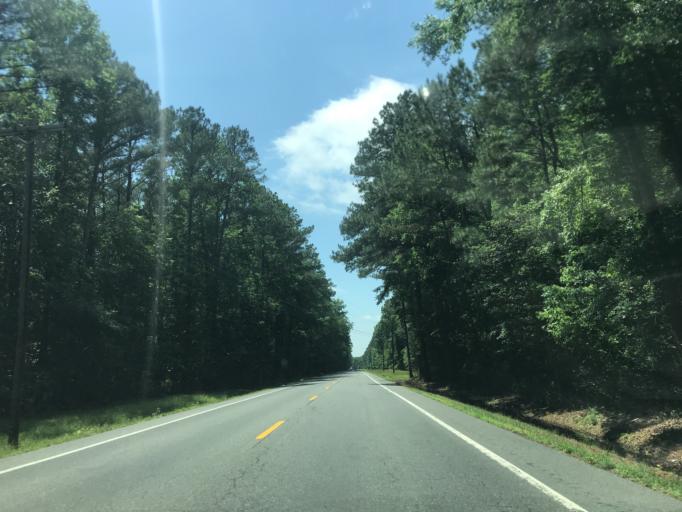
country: US
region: Maryland
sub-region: Dorchester County
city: Hurlock
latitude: 38.6330
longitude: -75.7968
